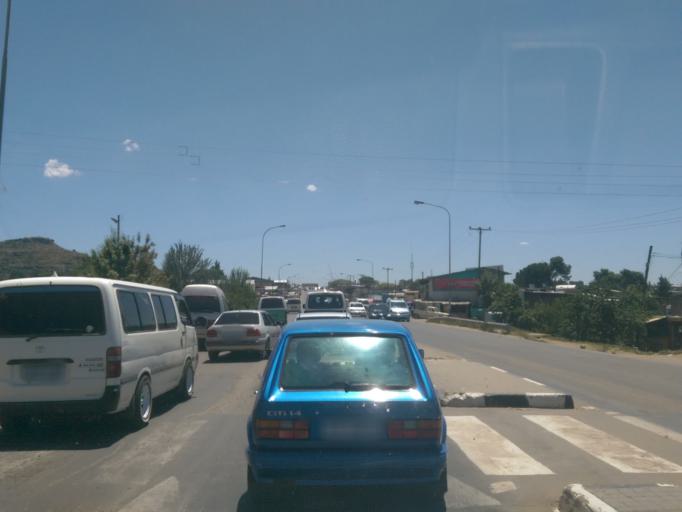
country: LS
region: Maseru
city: Maseru
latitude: -29.3418
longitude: 27.5143
